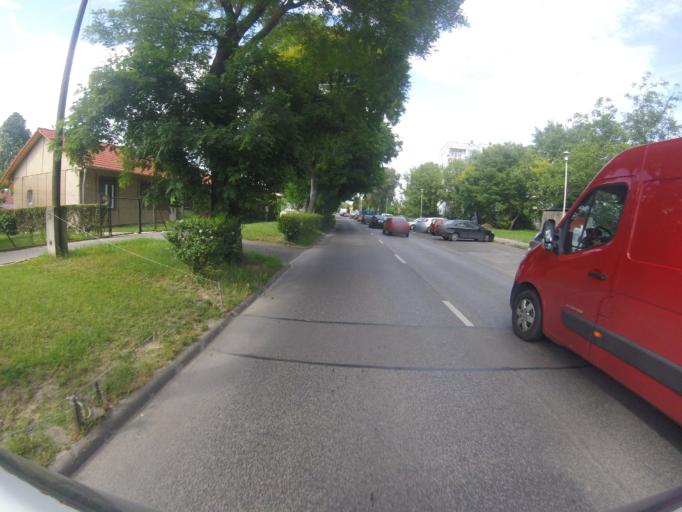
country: HU
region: Budapest
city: Budapest XXI. keruelet
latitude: 47.4100
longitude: 19.0688
